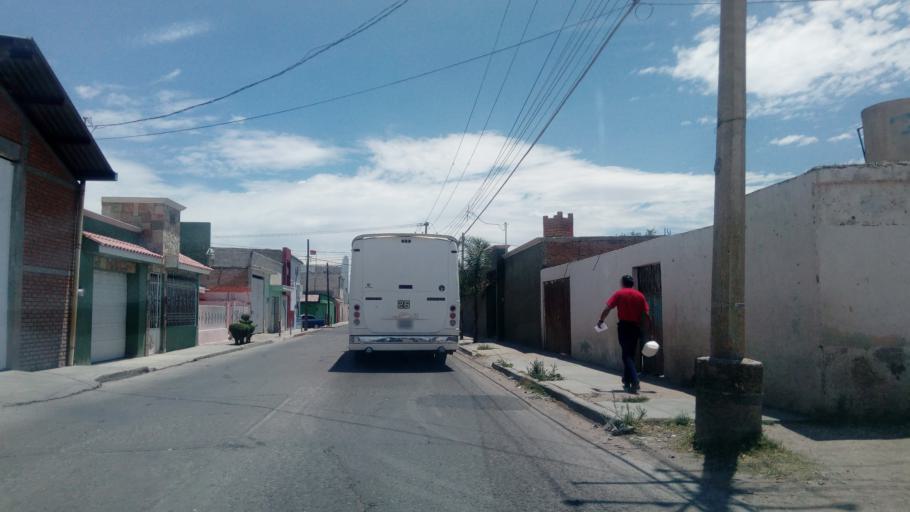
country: MX
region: Durango
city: Victoria de Durango
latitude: 24.0133
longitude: -104.6371
